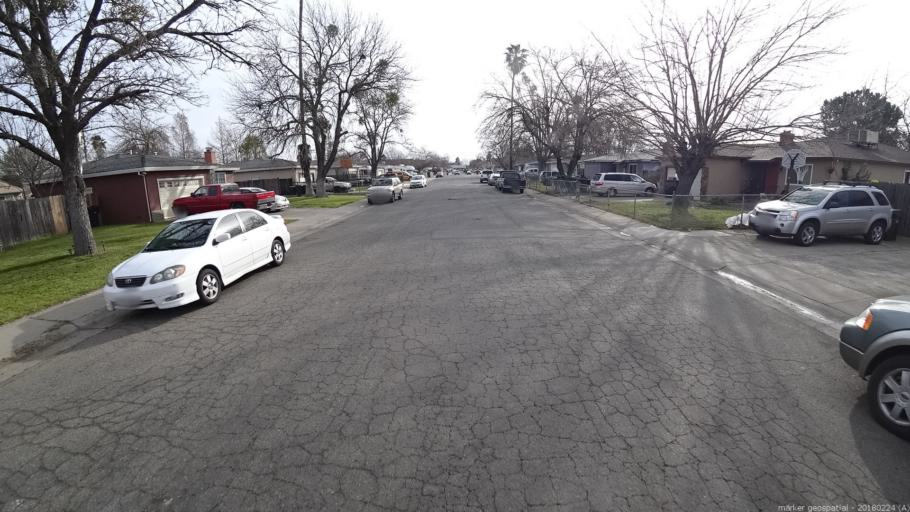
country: US
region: California
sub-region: Sacramento County
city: Rio Linda
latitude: 38.6864
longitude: -121.4629
